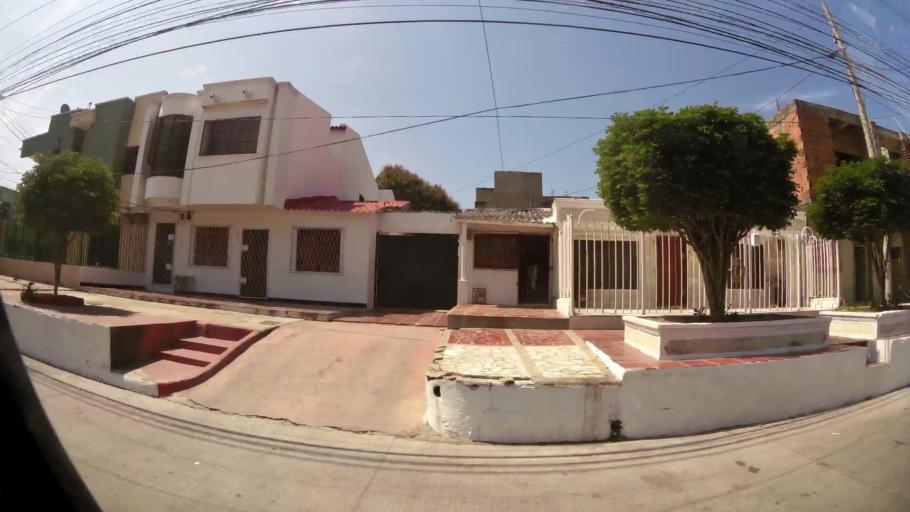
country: CO
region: Atlantico
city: Barranquilla
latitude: 10.9631
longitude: -74.7973
